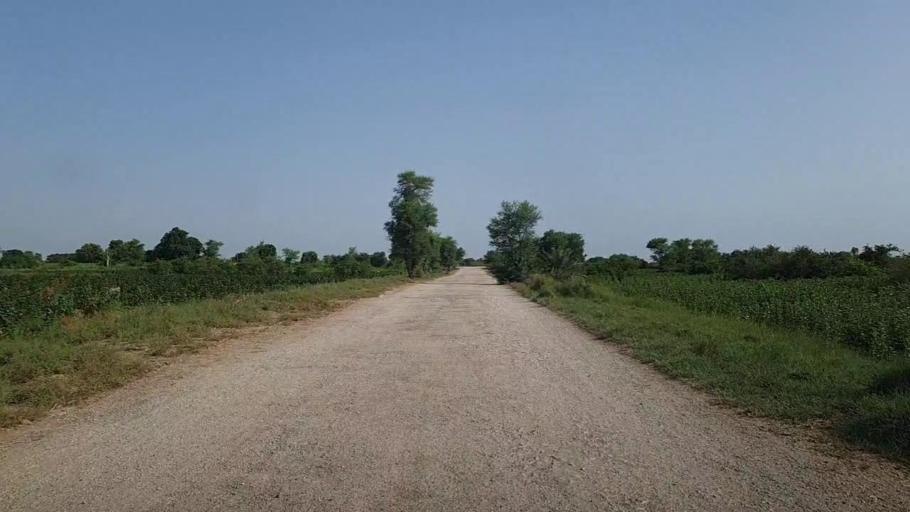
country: PK
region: Sindh
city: Karaundi
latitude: 26.8721
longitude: 68.3287
